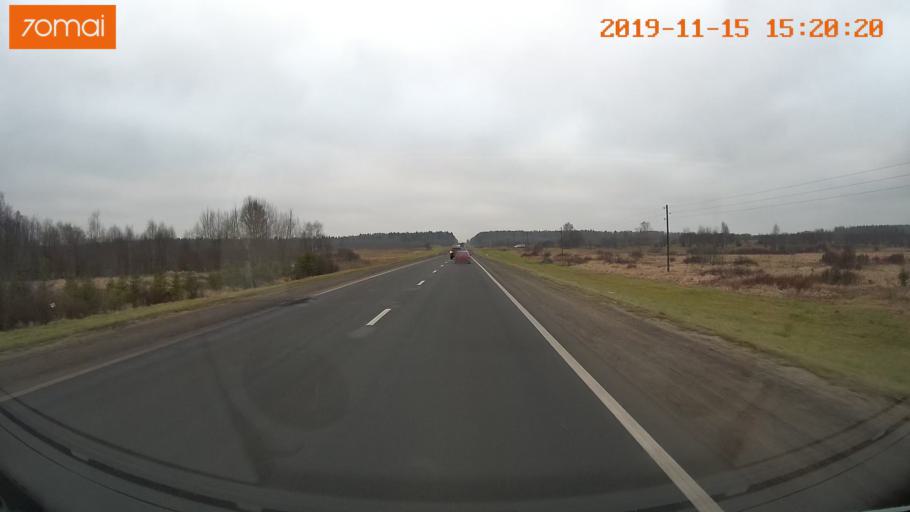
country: RU
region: Jaroslavl
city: Danilov
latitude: 58.2247
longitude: 40.1635
